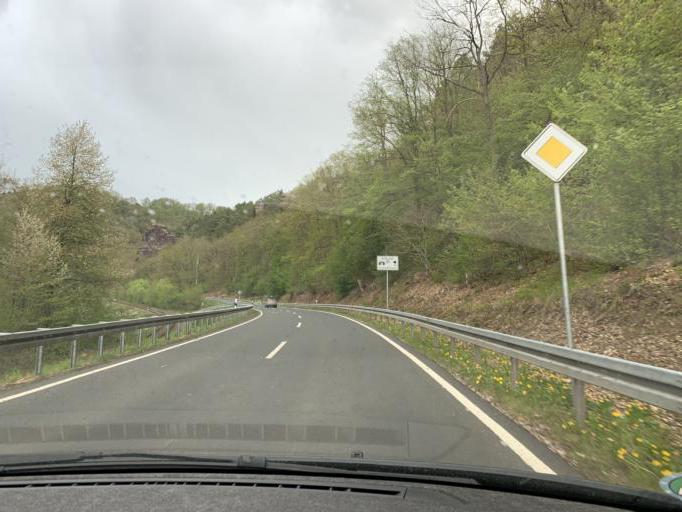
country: DE
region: North Rhine-Westphalia
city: Heimbach
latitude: 50.6557
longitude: 6.4968
